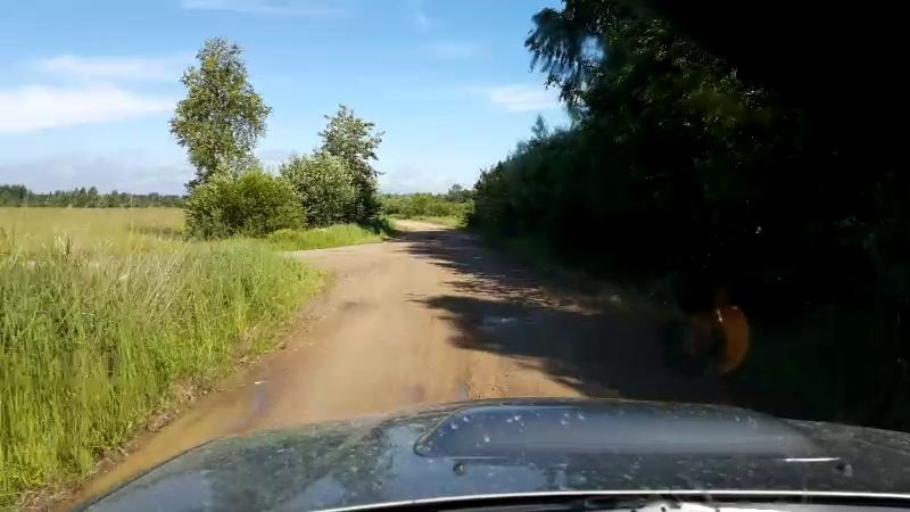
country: EE
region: Paernumaa
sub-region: Sindi linn
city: Sindi
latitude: 58.5036
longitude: 24.6985
